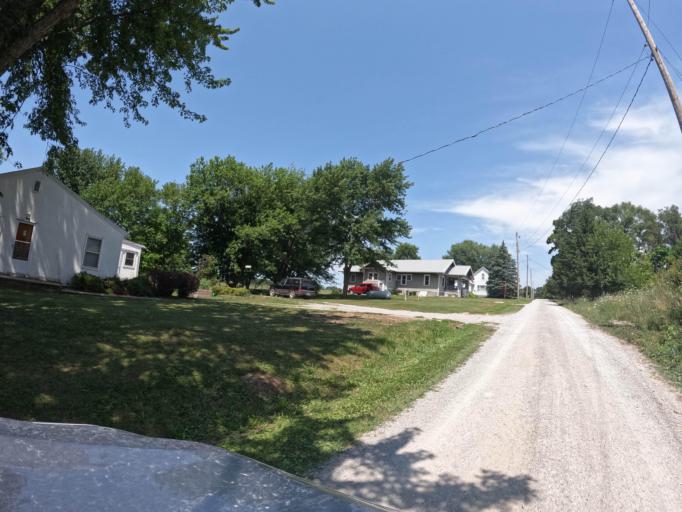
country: US
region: Iowa
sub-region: Appanoose County
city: Centerville
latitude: 40.7801
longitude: -92.9495
